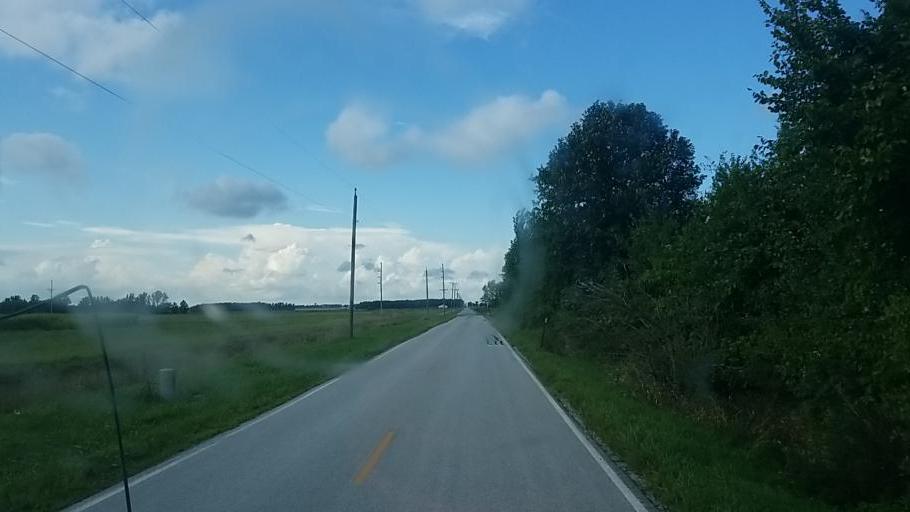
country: US
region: Ohio
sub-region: Hardin County
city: Forest
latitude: 40.7579
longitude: -83.4964
